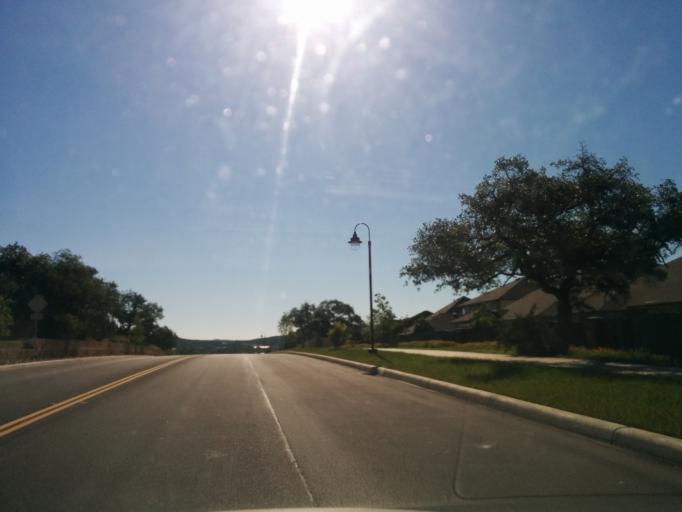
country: US
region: Texas
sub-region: Bexar County
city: Cross Mountain
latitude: 29.6767
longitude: -98.6464
